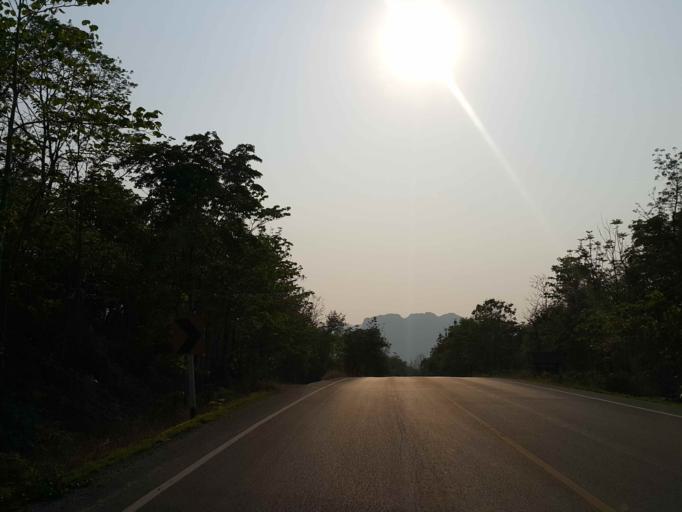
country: TH
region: Sukhothai
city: Thung Saliam
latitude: 17.3495
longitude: 99.4207
